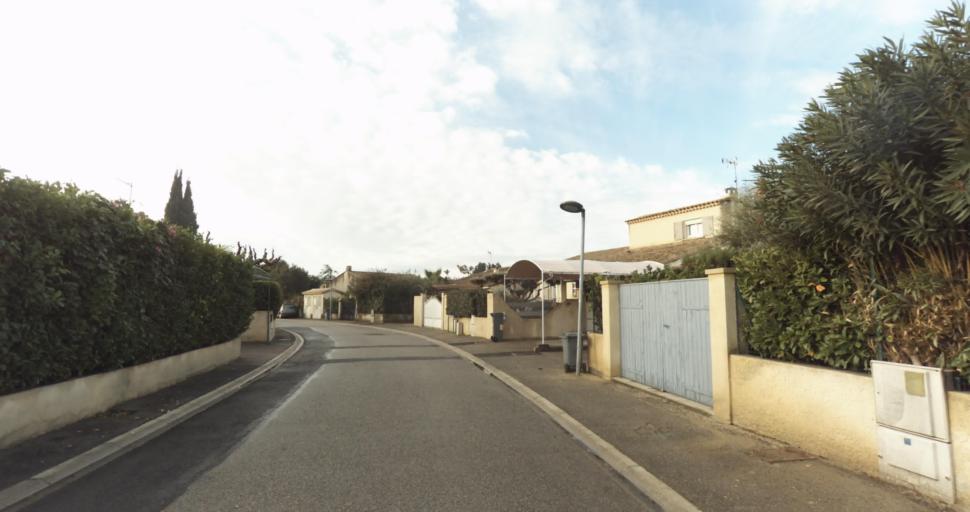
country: FR
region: Provence-Alpes-Cote d'Azur
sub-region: Departement des Bouches-du-Rhone
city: Rognonas
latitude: 43.9087
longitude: 4.8036
